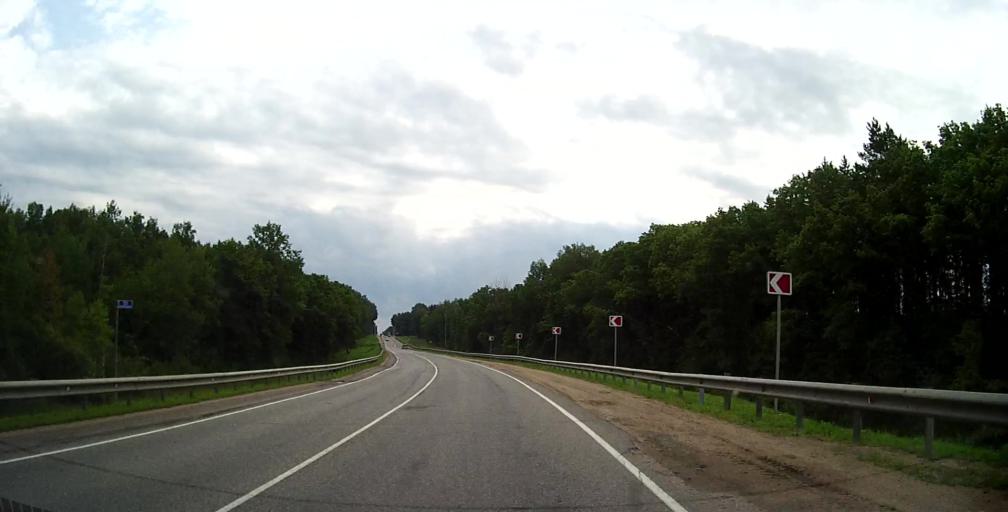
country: RU
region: Smolensk
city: Katyn'
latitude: 54.7660
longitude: 31.7128
